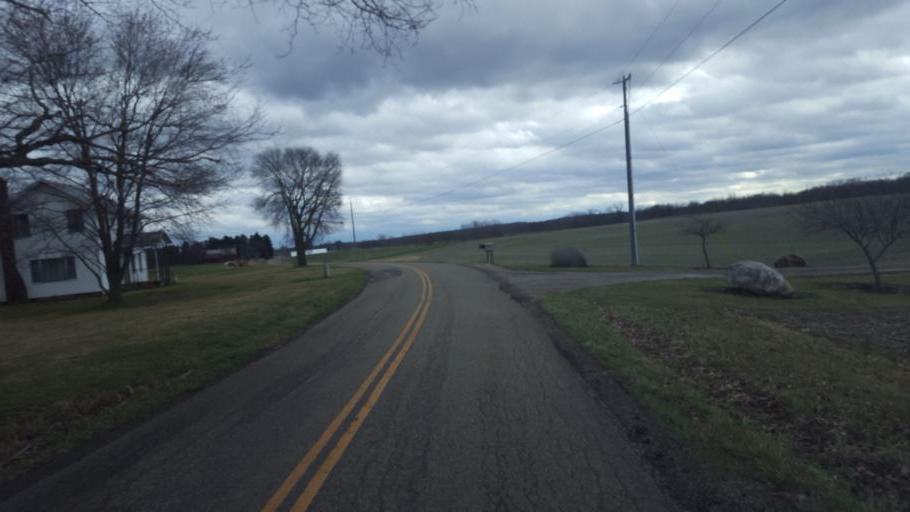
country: US
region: Ohio
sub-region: Licking County
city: Utica
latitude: 40.2668
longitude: -82.4850
